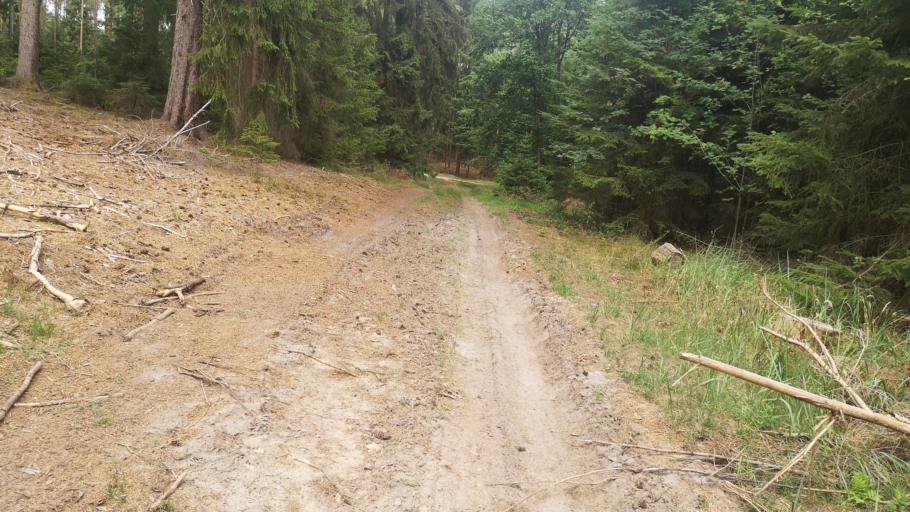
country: DE
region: Lower Saxony
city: Thomasburg
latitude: 53.2428
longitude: 10.6945
